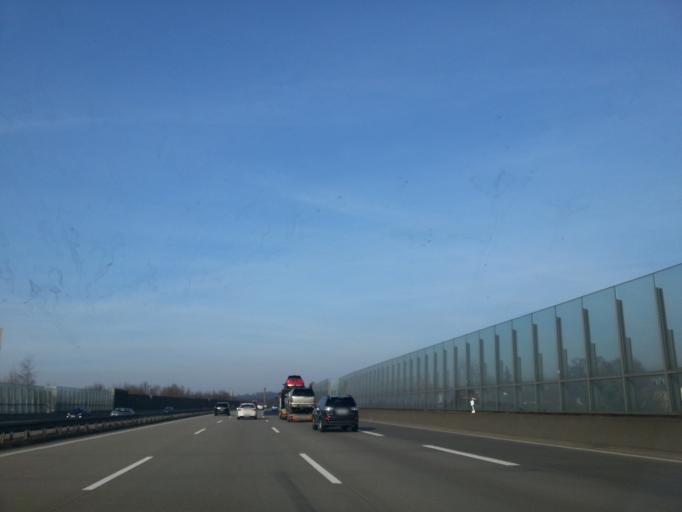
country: DE
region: Saxony
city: Radebeul
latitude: 51.0890
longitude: 13.6927
